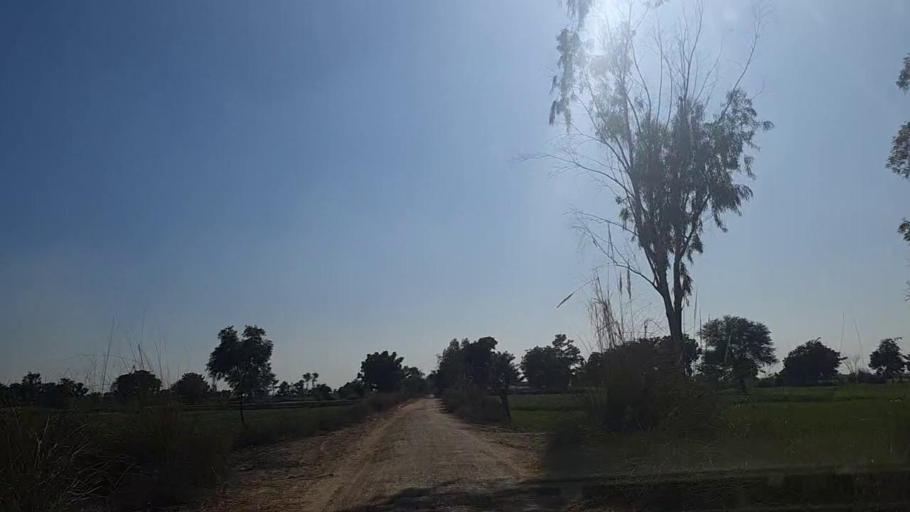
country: PK
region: Sindh
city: Sakrand
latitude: 26.2448
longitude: 68.2000
